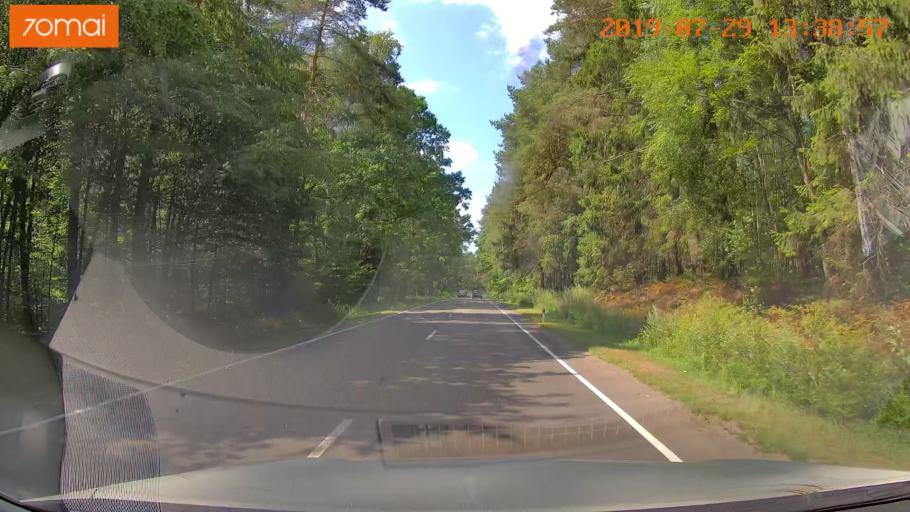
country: RU
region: Kaliningrad
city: Svetlyy
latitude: 54.7229
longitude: 20.1622
